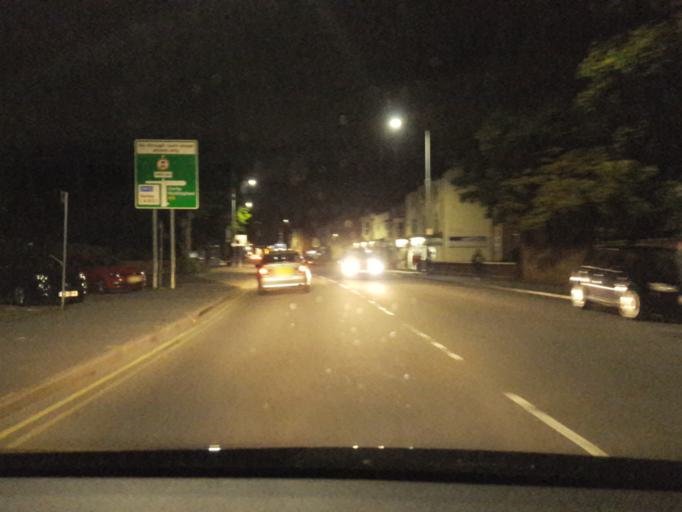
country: GB
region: England
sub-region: Leicestershire
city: Loughborough
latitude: 52.7682
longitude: -1.2013
